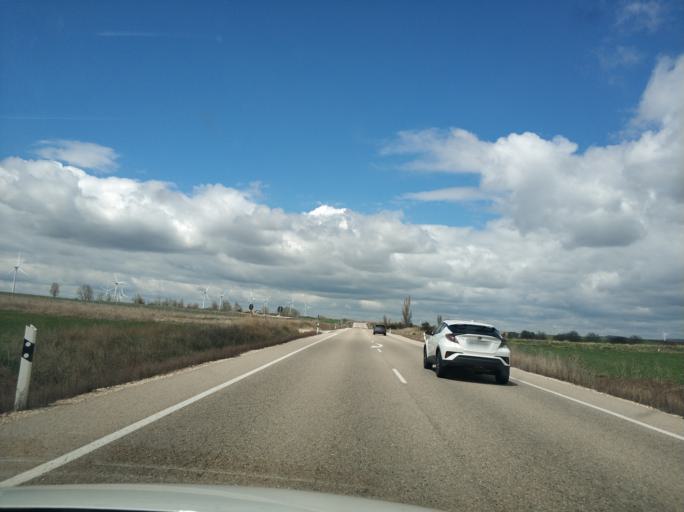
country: ES
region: Castille and Leon
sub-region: Provincia de Burgos
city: Hontoria de la Cantera
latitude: 42.1947
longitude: -3.6439
